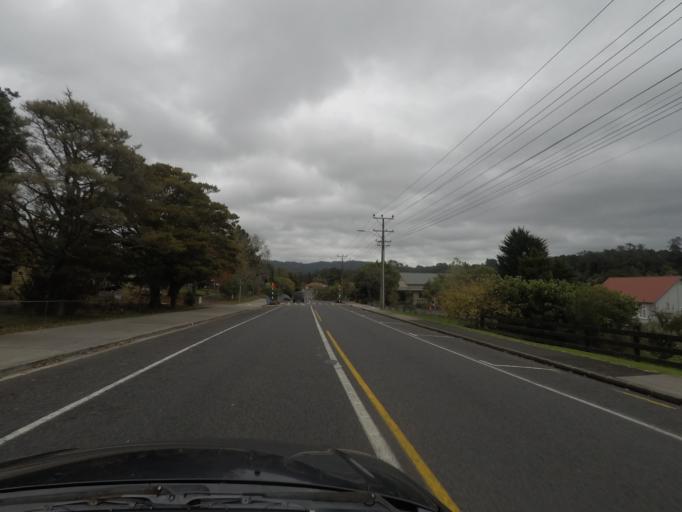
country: NZ
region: Auckland
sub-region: Auckland
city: Waitakere
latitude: -36.9110
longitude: 174.6220
